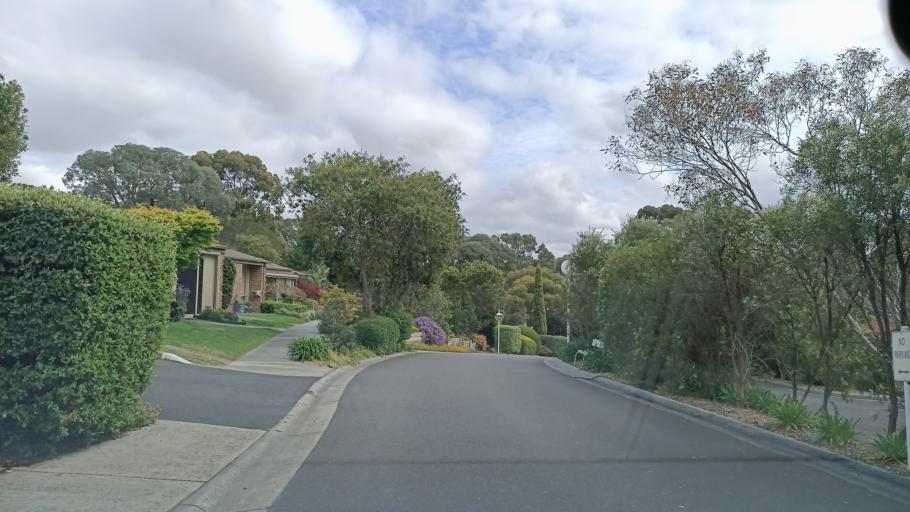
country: AU
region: Victoria
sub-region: Monash
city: Mulgrave
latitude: -37.9216
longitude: 145.1936
